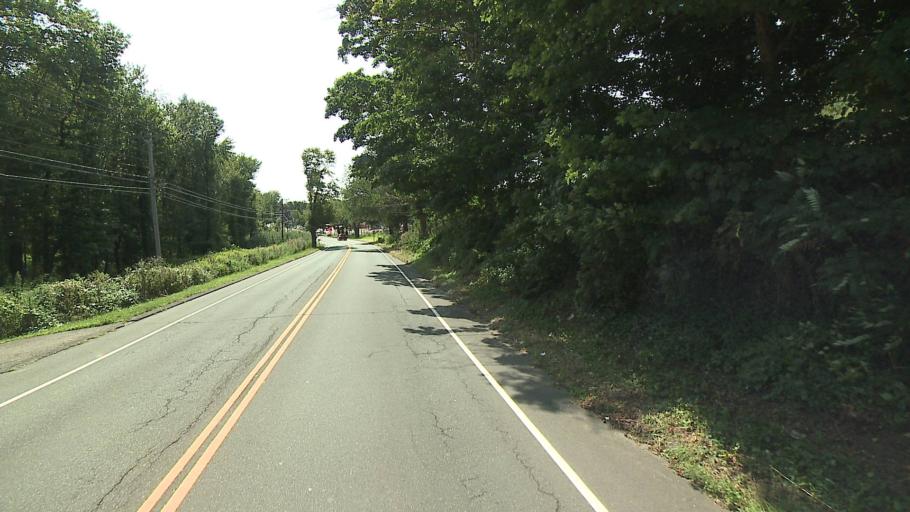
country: US
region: Connecticut
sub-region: Fairfield County
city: Trumbull
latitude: 41.2521
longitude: -73.2806
